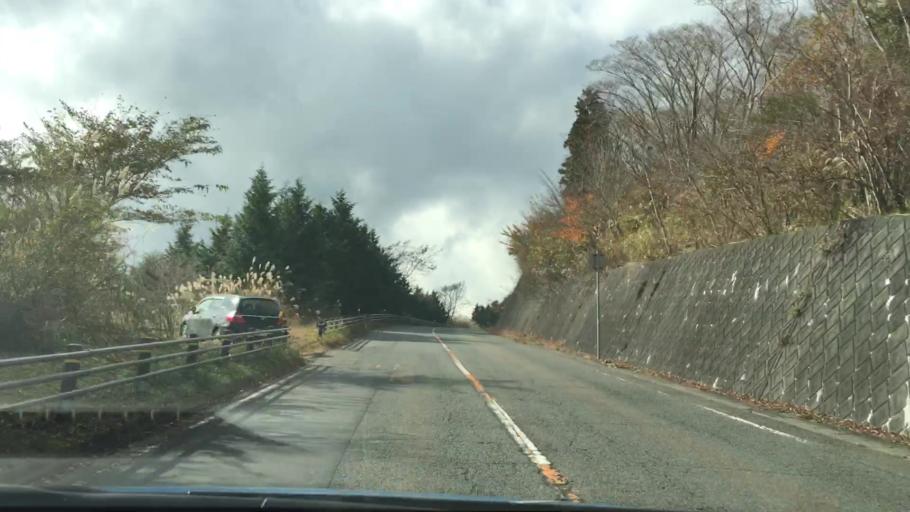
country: JP
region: Shizuoka
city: Gotemba
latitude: 35.3991
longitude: 138.9386
